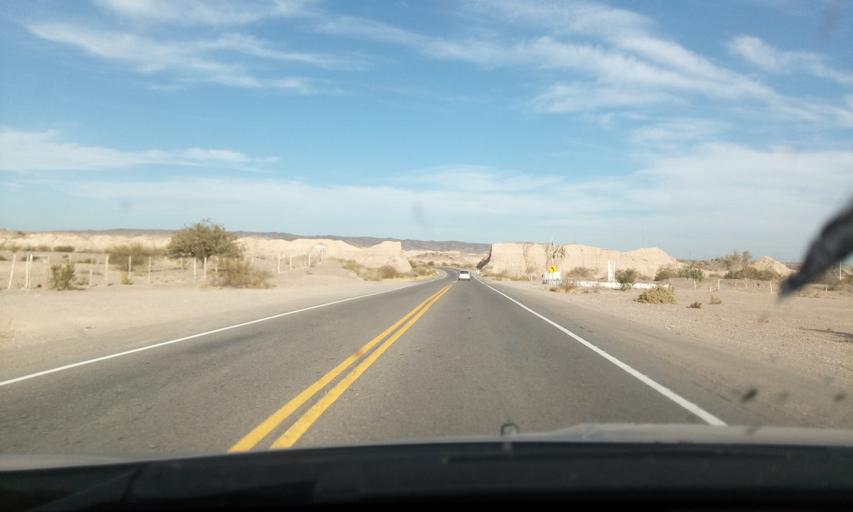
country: AR
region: San Juan
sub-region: Departamento de Rivadavia
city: Rivadavia
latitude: -31.4438
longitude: -68.6522
